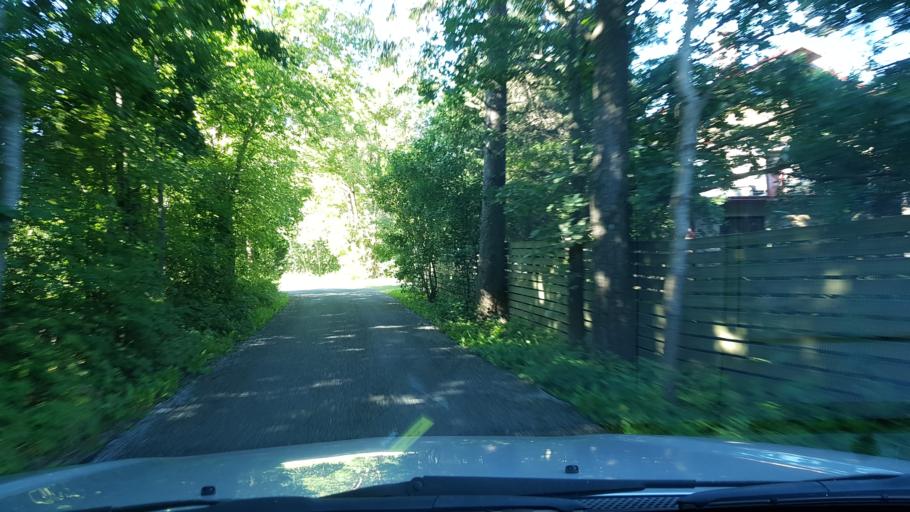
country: EE
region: Harju
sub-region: Joelaehtme vald
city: Loo
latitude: 59.4318
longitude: 24.9305
